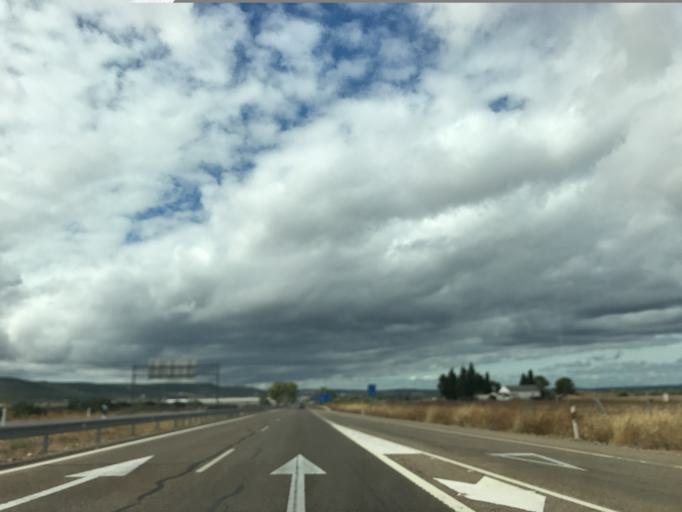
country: ES
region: Andalusia
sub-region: Province of Cordoba
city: Villa del Rio
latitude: 37.9892
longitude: -4.2628
